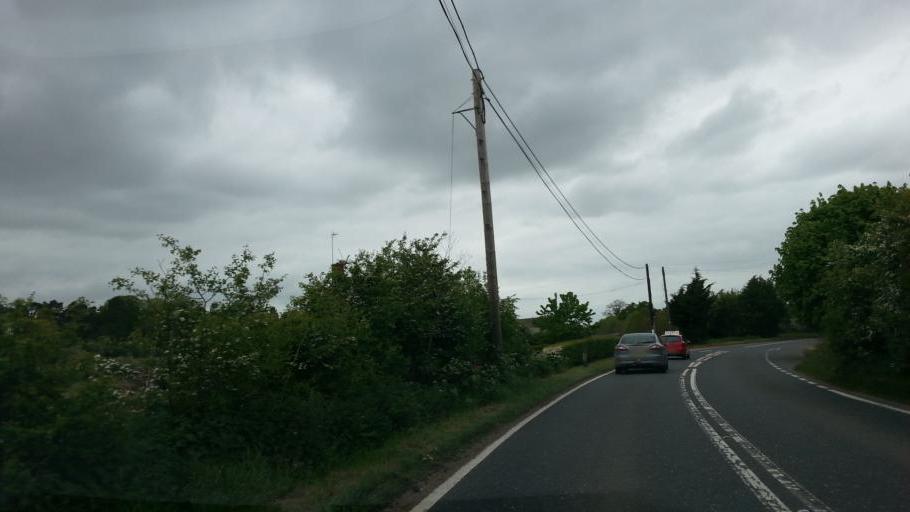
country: GB
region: England
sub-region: Suffolk
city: Bury St Edmunds
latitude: 52.2988
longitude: 0.6314
